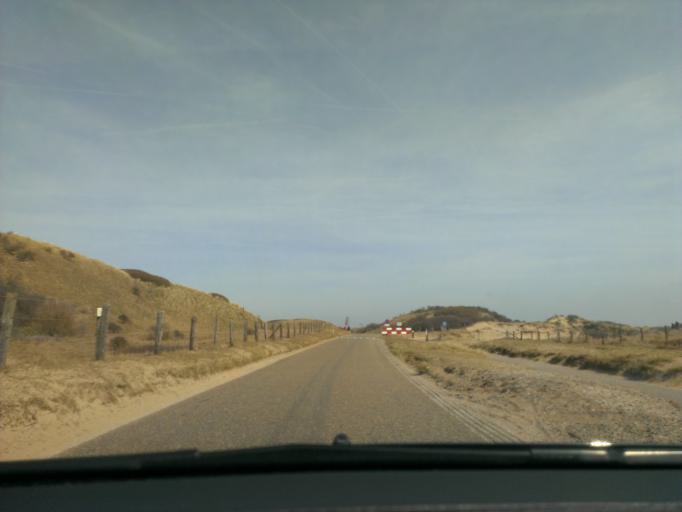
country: NL
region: North Holland
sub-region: Gemeente Zandvoort
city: Zandvoort
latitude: 52.4142
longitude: 4.5527
